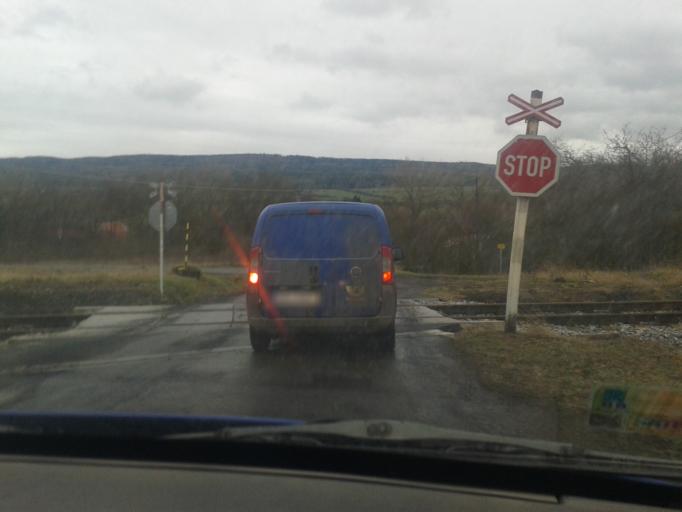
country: CZ
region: Central Bohemia
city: Revnice
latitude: 49.8889
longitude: 14.1484
